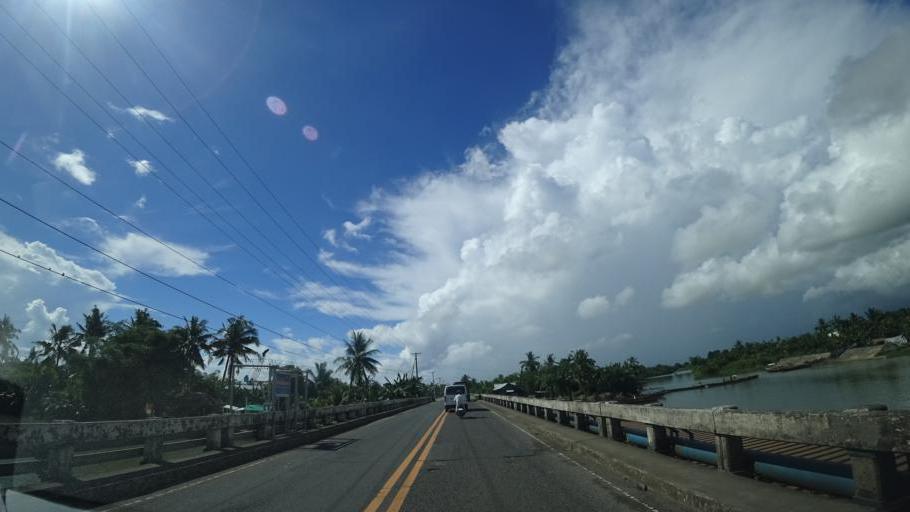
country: PH
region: Eastern Visayas
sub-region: Province of Leyte
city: Palo
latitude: 11.1463
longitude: 125.0021
